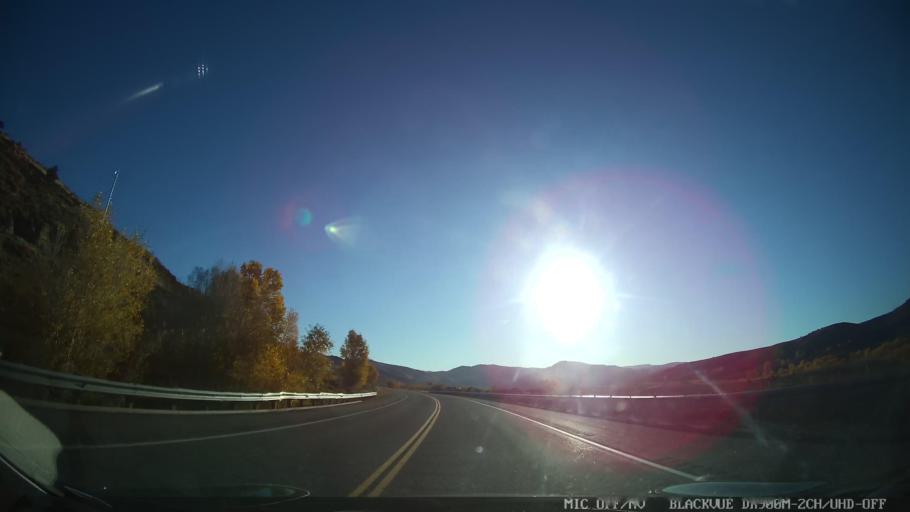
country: US
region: Colorado
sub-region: Grand County
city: Hot Sulphur Springs
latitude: 40.0514
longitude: -106.1695
